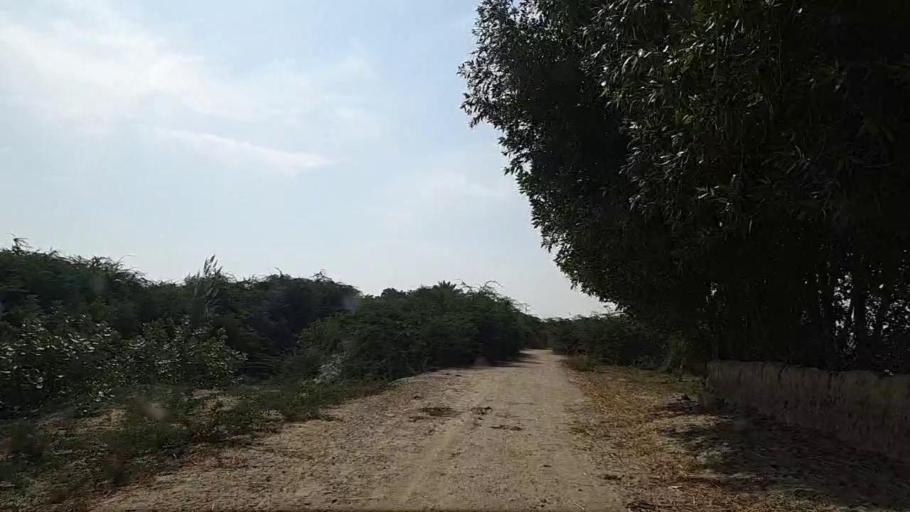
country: PK
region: Sindh
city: Daro Mehar
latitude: 24.7049
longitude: 68.1580
